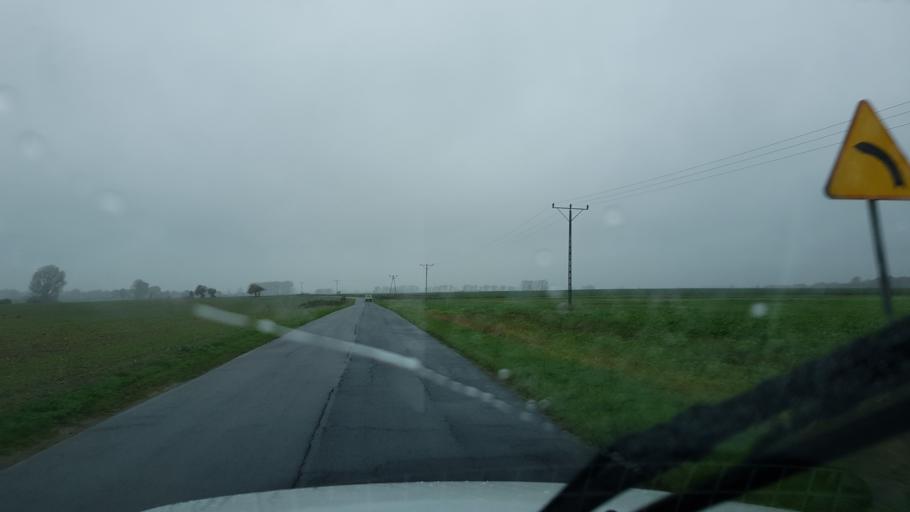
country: PL
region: West Pomeranian Voivodeship
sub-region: Powiat pyrzycki
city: Pyrzyce
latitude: 53.1567
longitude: 14.8677
